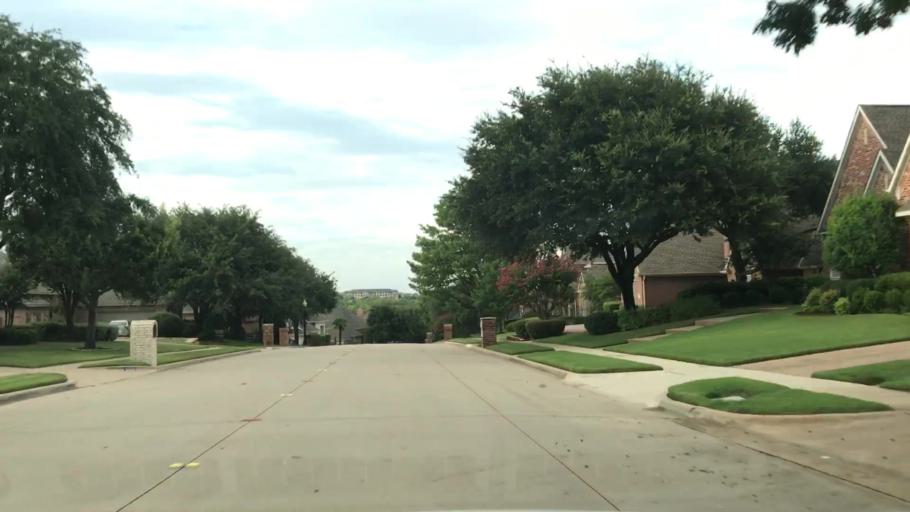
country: US
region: Texas
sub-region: Denton County
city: The Colony
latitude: 33.0411
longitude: -96.8501
